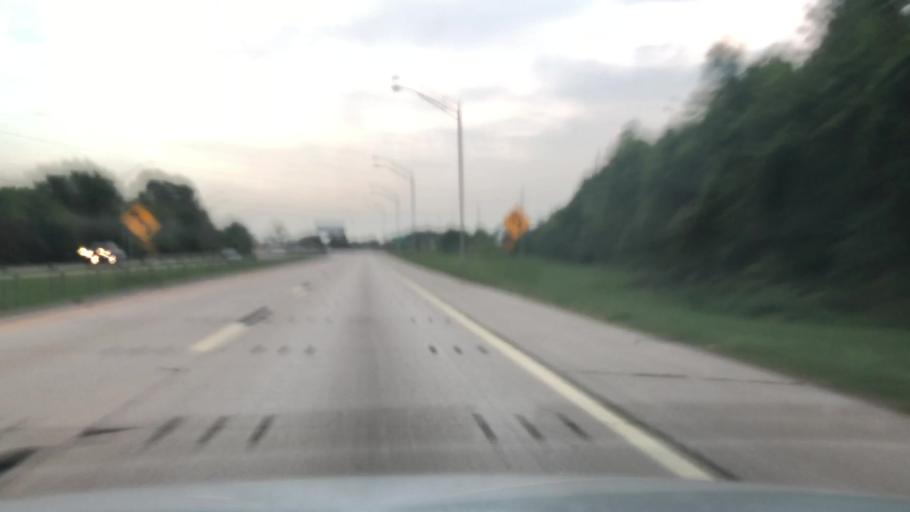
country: US
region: Oklahoma
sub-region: Tulsa County
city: Tulsa
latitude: 36.1836
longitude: -95.9633
